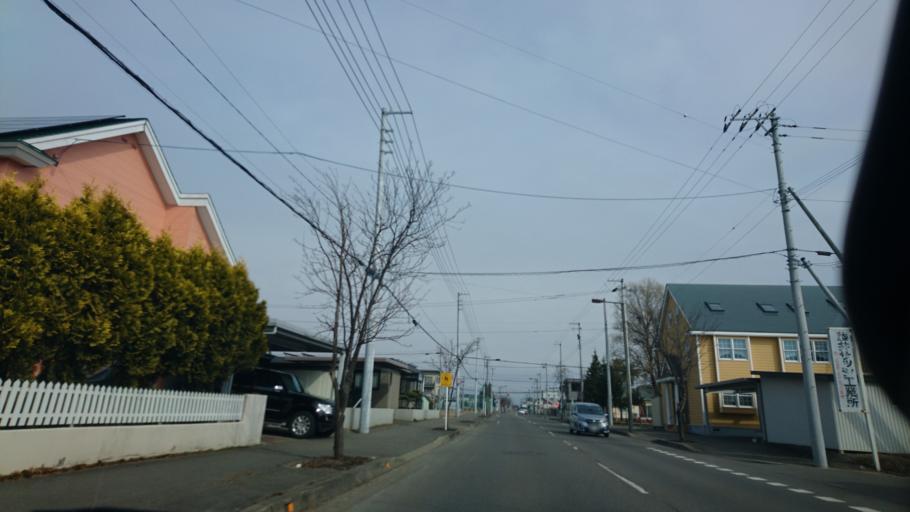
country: JP
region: Hokkaido
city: Otofuke
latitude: 42.9664
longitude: 143.2131
